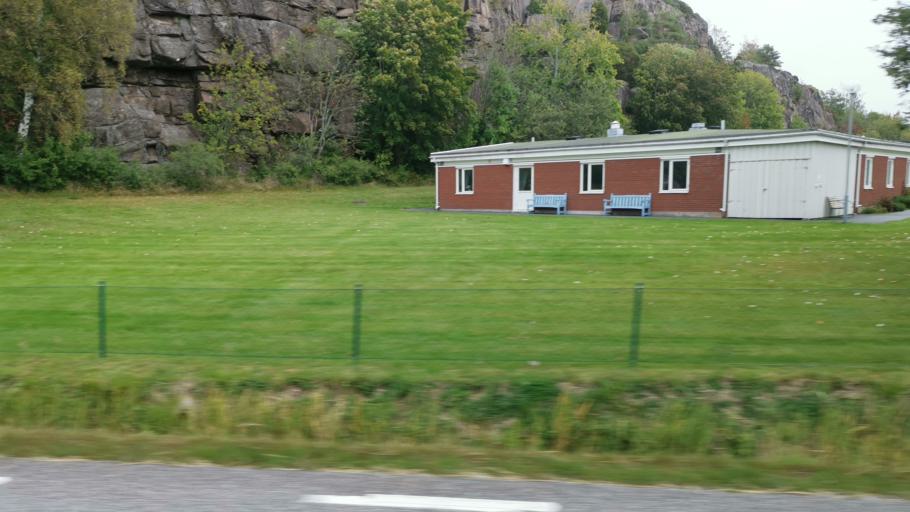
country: SE
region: Vaestra Goetaland
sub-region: Sotenas Kommun
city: Hunnebostrand
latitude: 58.5694
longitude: 11.3570
